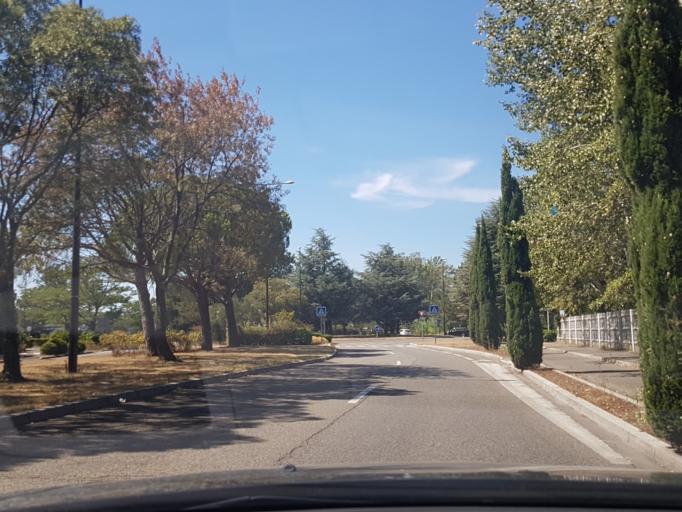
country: FR
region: Provence-Alpes-Cote d'Azur
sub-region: Departement des Bouches-du-Rhone
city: Rognonas
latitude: 43.9211
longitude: 4.8039
